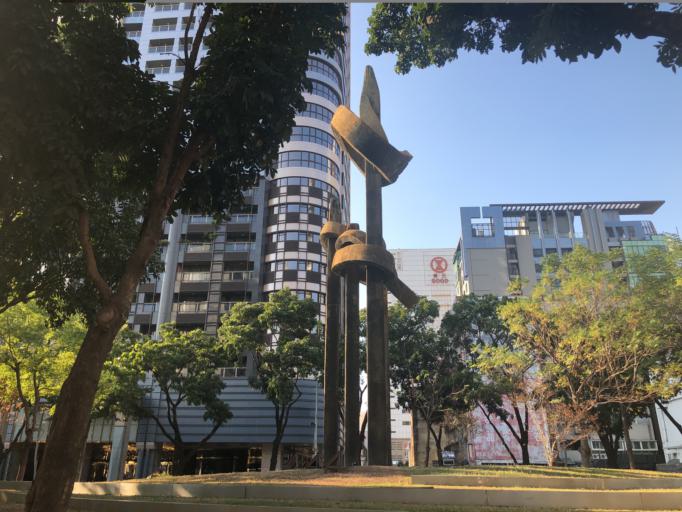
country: TW
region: Taiwan
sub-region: Taichung City
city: Taichung
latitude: 24.1539
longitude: 120.6638
